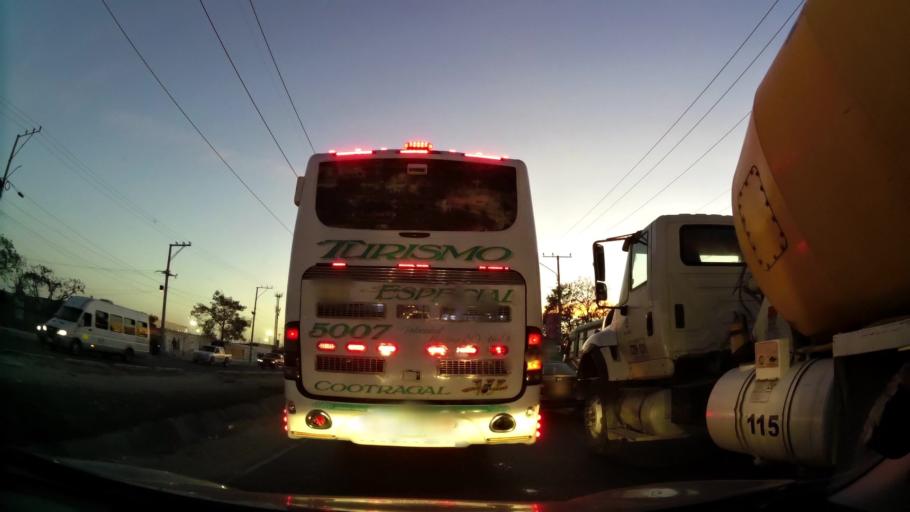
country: CO
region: Atlantico
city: Soledad
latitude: 10.9304
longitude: -74.7842
